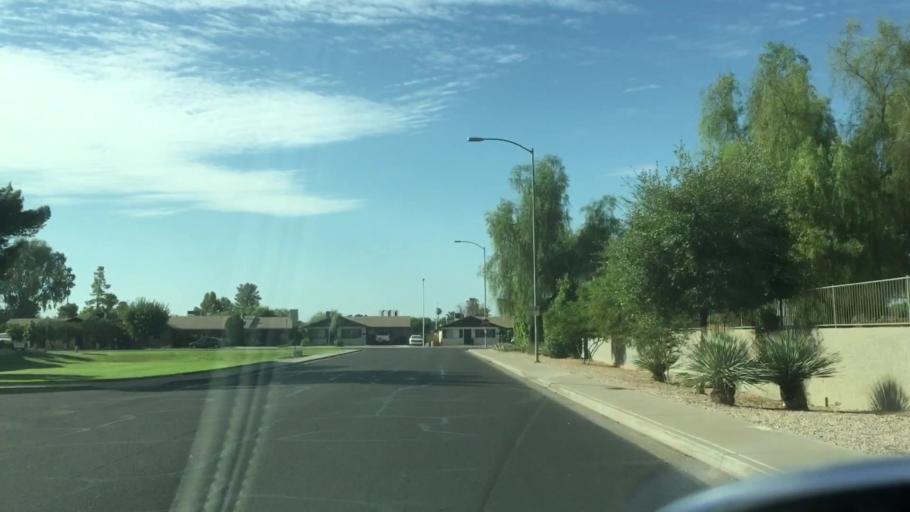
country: US
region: Arizona
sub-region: Maricopa County
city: Mesa
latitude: 33.4014
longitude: -111.8443
